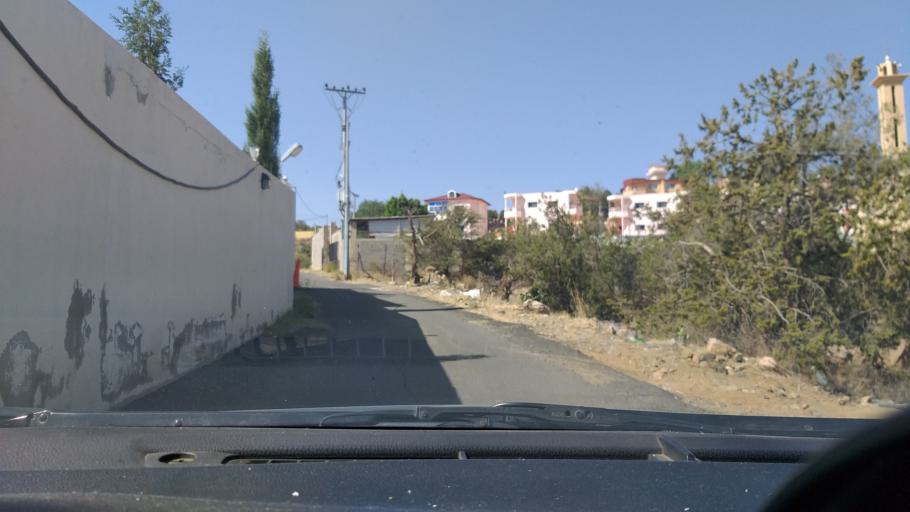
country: SA
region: Makkah
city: Ash Shafa
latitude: 21.0638
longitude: 40.3234
